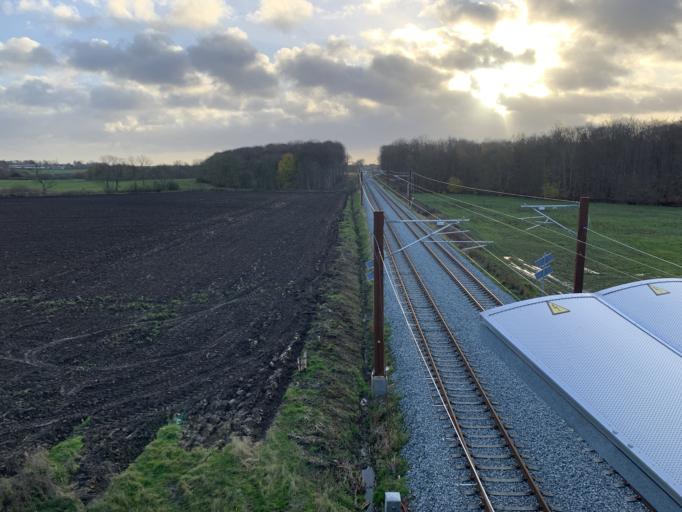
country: DK
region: Zealand
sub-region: Naestved Kommune
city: Fensmark
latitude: 55.3349
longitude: 11.7229
